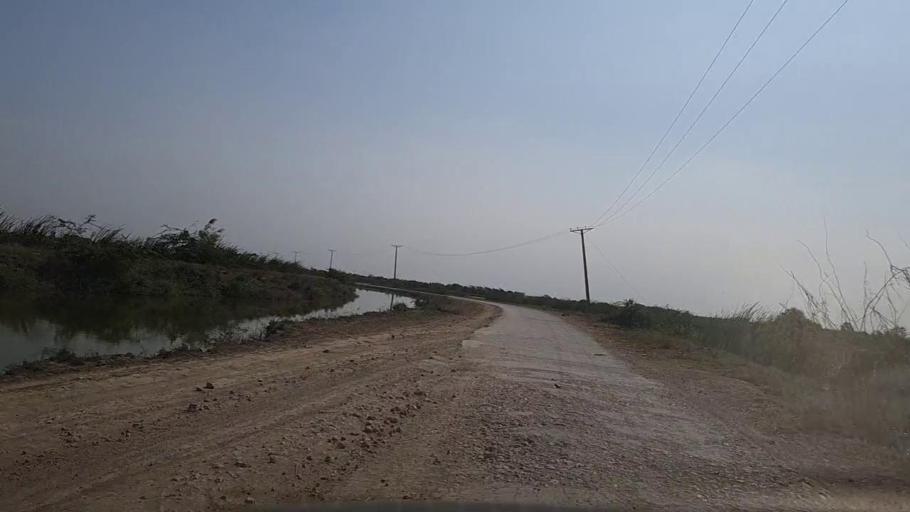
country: PK
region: Sindh
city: Thatta
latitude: 24.5845
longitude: 67.9088
